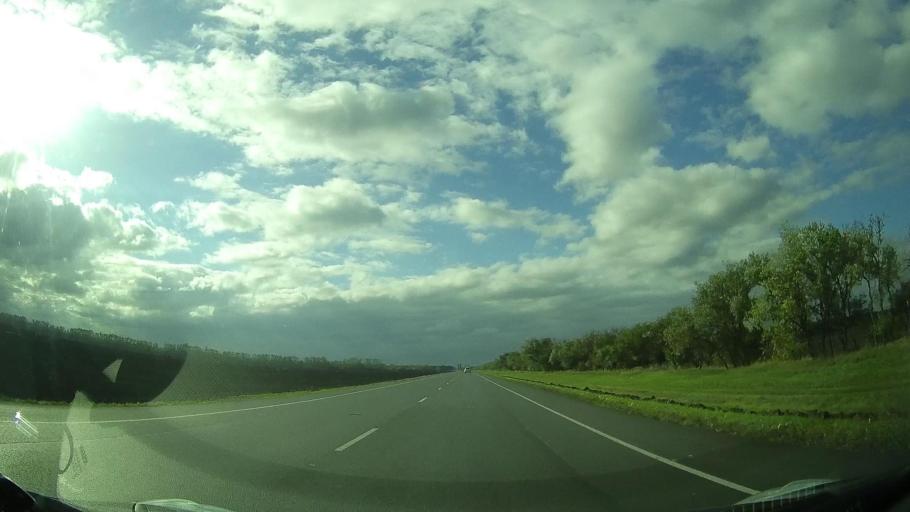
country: RU
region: Rostov
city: Tselina
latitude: 46.5327
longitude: 40.9318
